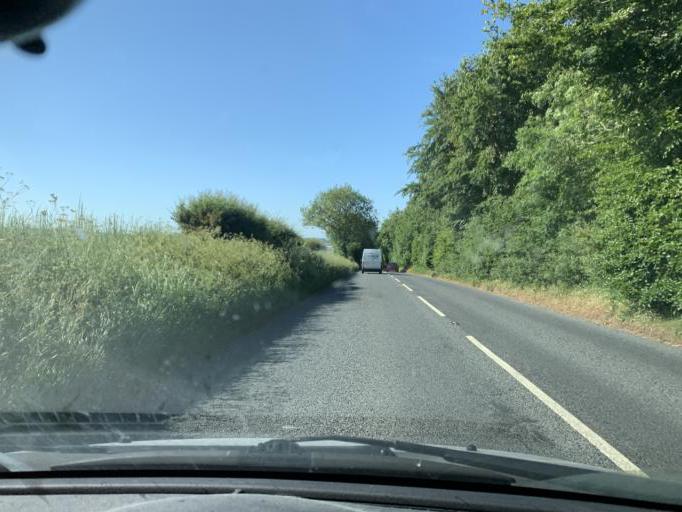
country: GB
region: England
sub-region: Wiltshire
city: Durnford
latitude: 51.1238
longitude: -1.7873
